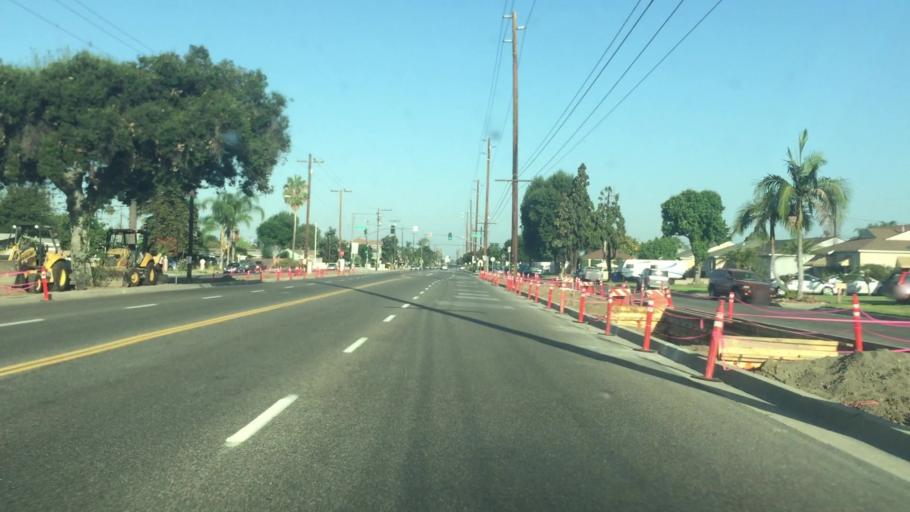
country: US
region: California
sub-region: Los Angeles County
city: Irwindale
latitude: 34.0960
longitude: -117.9277
